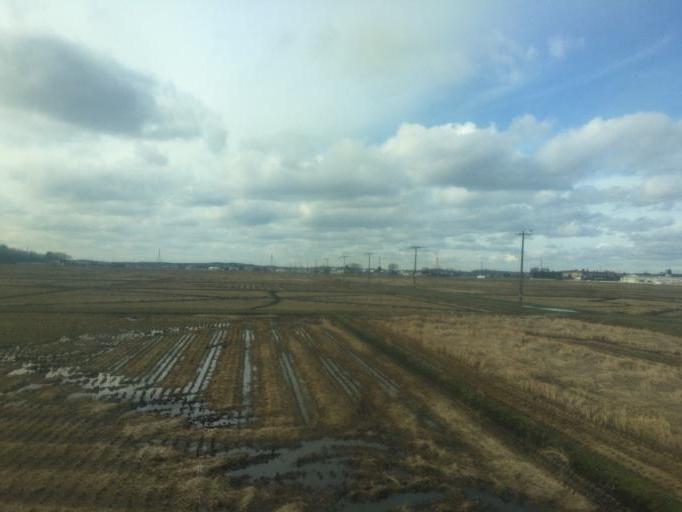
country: JP
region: Akita
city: Noshiromachi
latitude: 40.1787
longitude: 140.0587
